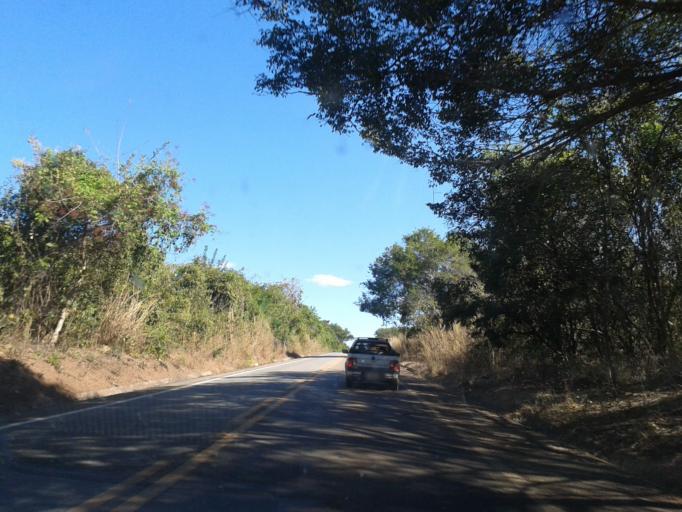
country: BR
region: Goias
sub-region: Mozarlandia
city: Mozarlandia
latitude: -14.4181
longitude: -50.4497
